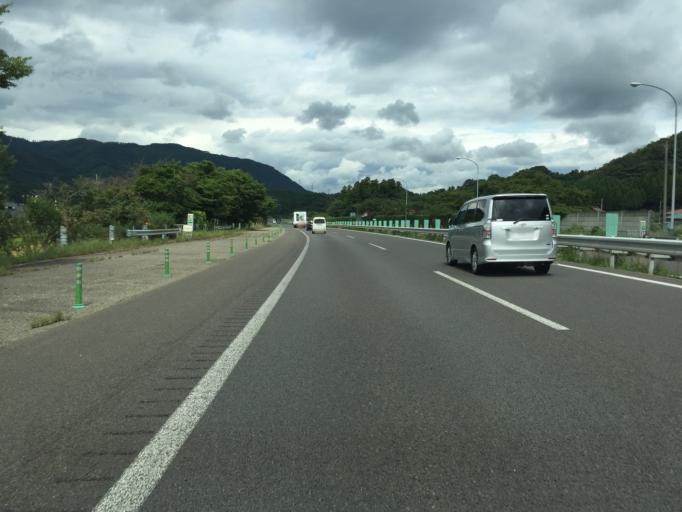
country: JP
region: Miyagi
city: Shiroishi
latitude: 37.9289
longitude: 140.6103
